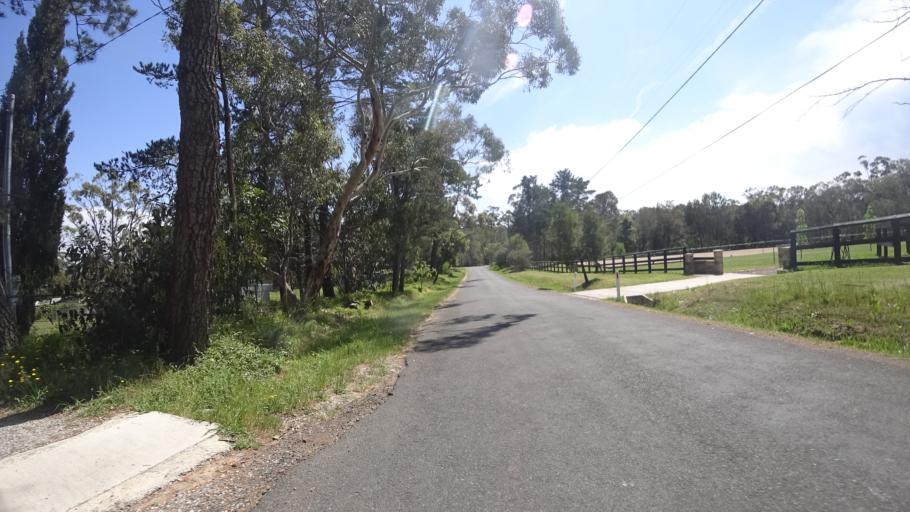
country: AU
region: New South Wales
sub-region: City of Sydney
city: North Turramurra
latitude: -33.6749
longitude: 151.1849
